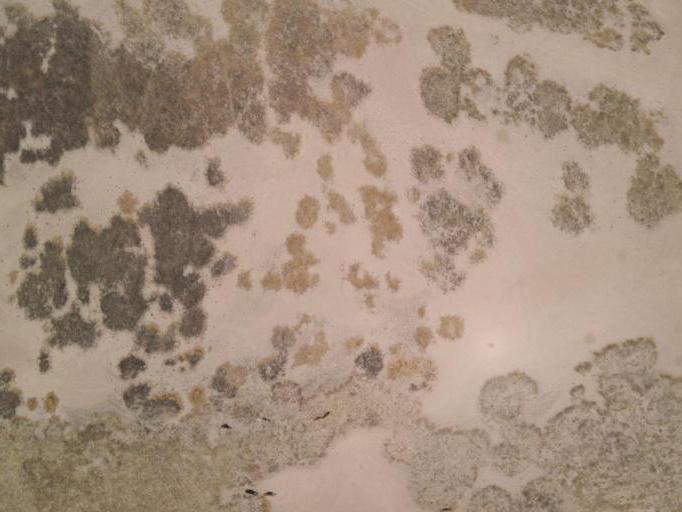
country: BO
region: La Paz
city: Batallas
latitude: -16.3537
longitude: -68.6301
